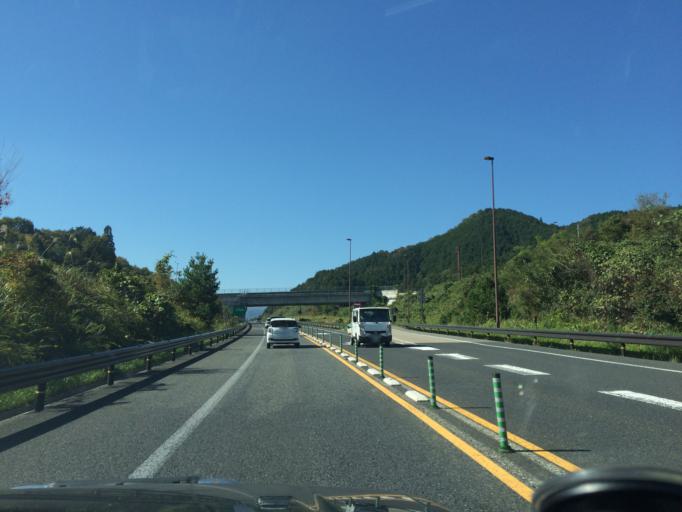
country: JP
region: Hyogo
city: Toyooka
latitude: 35.3101
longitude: 134.8720
